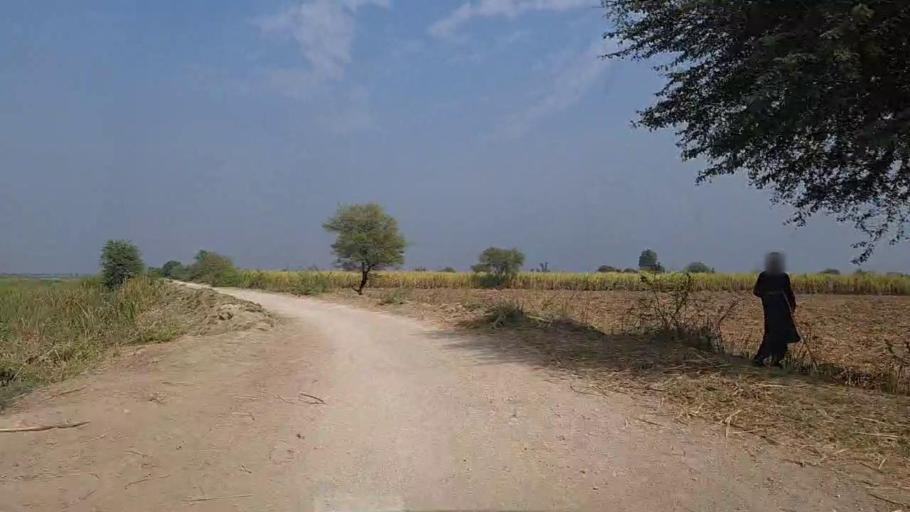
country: PK
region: Sindh
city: Mirwah Gorchani
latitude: 25.3731
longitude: 69.0378
